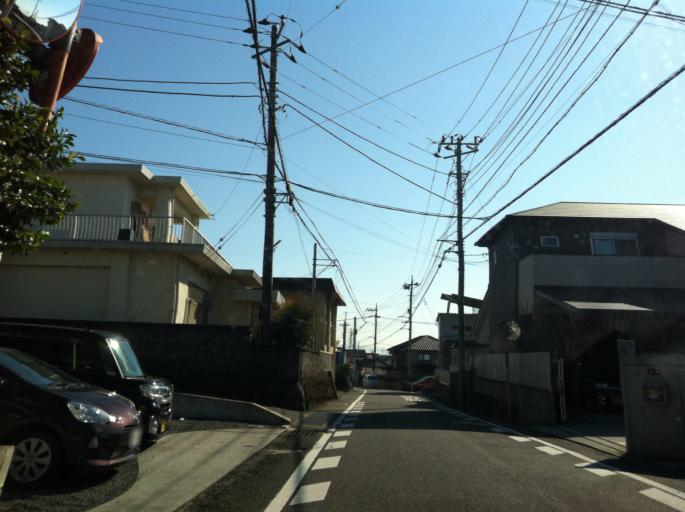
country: JP
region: Shizuoka
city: Fuji
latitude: 35.1588
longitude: 138.7472
